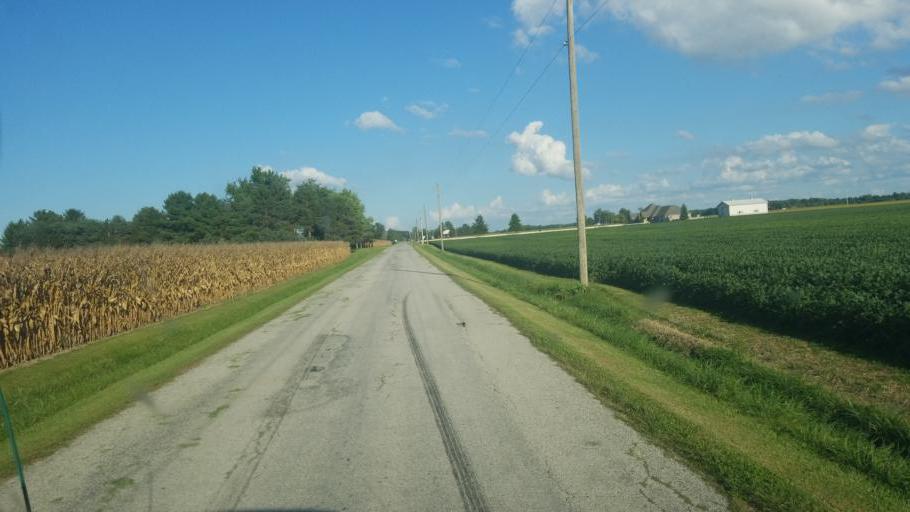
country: US
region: Ohio
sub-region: Hancock County
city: Arlington
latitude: 40.9353
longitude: -83.5750
